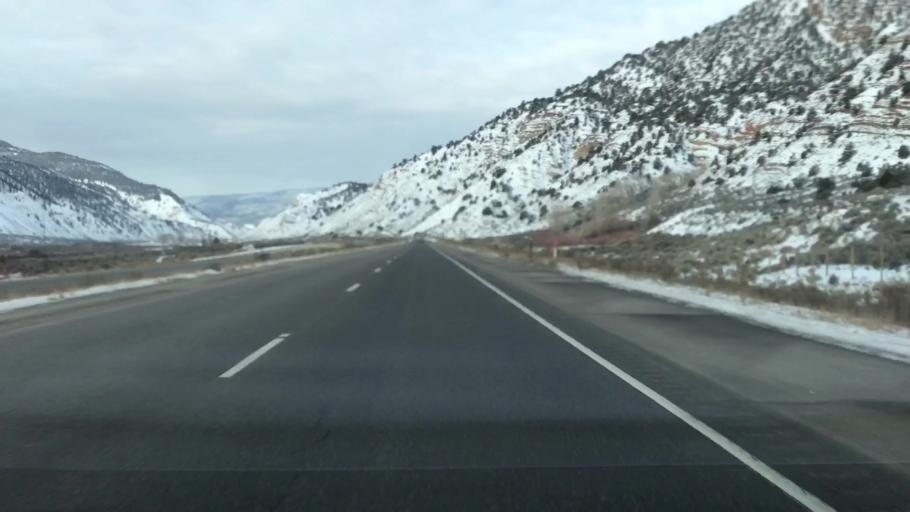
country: US
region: Colorado
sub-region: Eagle County
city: Gypsum
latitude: 39.6491
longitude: -107.0038
